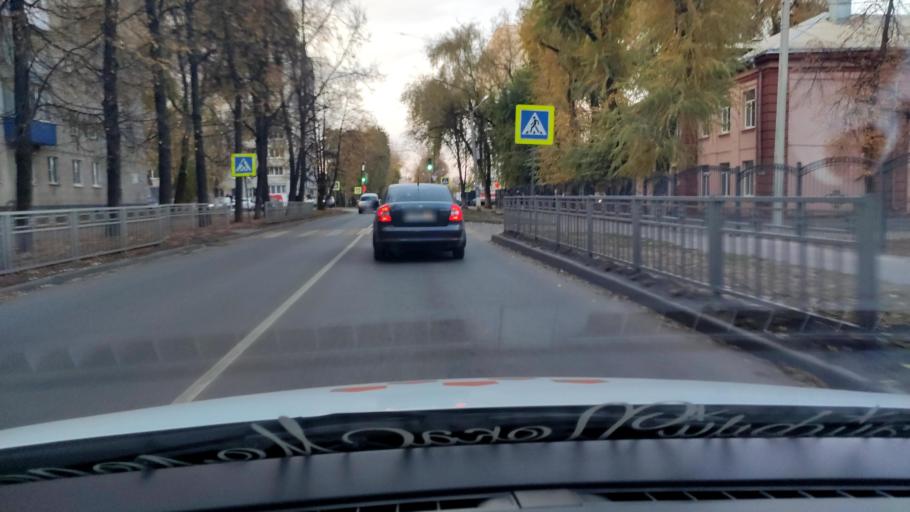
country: RU
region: Voronezj
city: Voronezh
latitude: 51.6862
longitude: 39.1907
